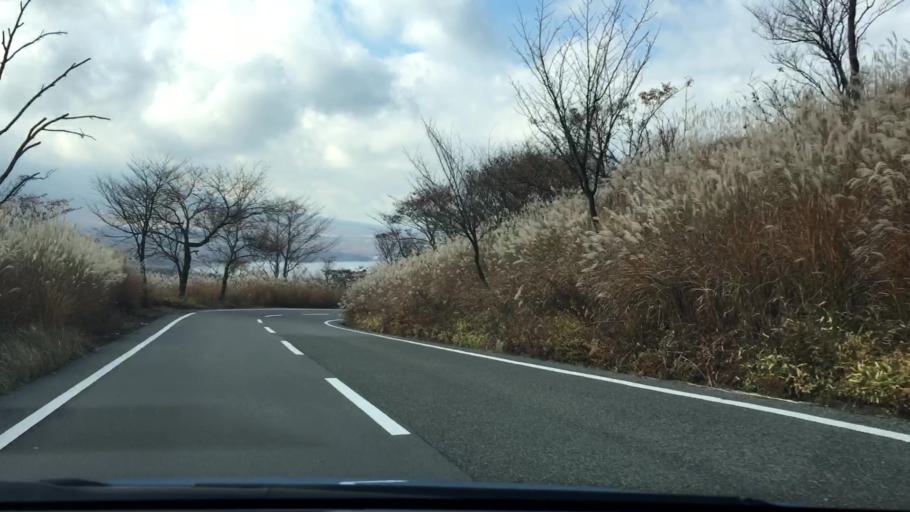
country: JP
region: Shizuoka
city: Gotemba
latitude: 35.4081
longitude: 138.9136
